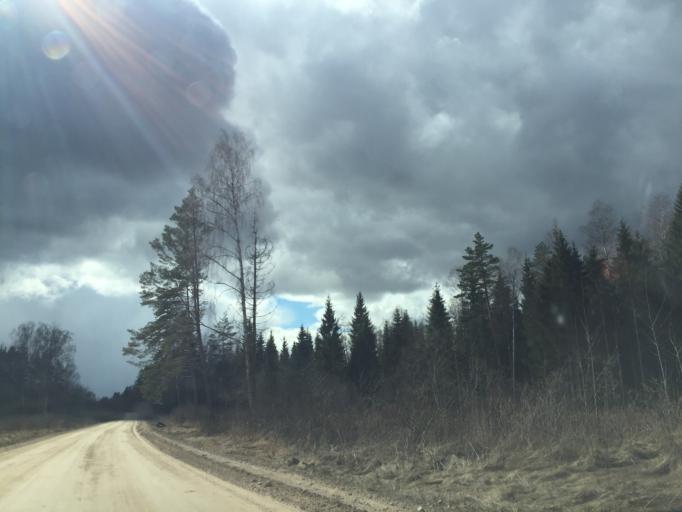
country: LV
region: Akniste
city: Akniste
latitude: 56.1114
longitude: 25.8316
